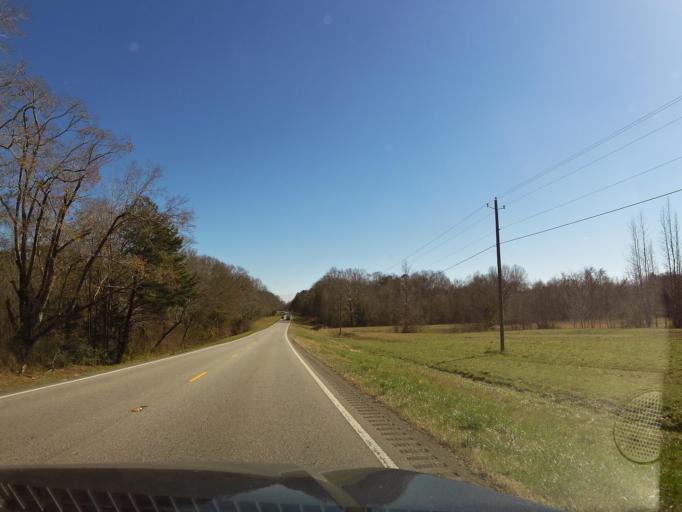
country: US
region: Alabama
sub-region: Bullock County
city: Union Springs
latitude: 32.1052
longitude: -85.5764
